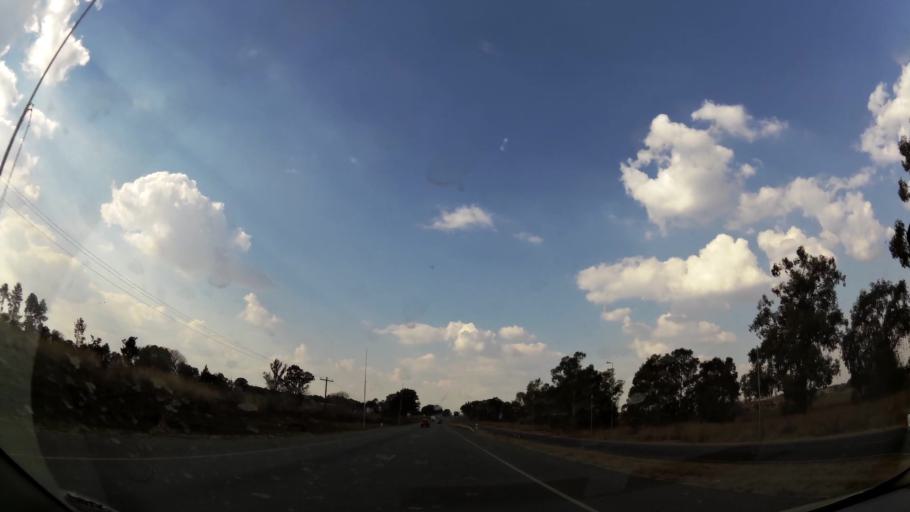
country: ZA
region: Gauteng
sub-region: Ekurhuleni Metropolitan Municipality
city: Boksburg
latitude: -26.2646
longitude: 28.3015
